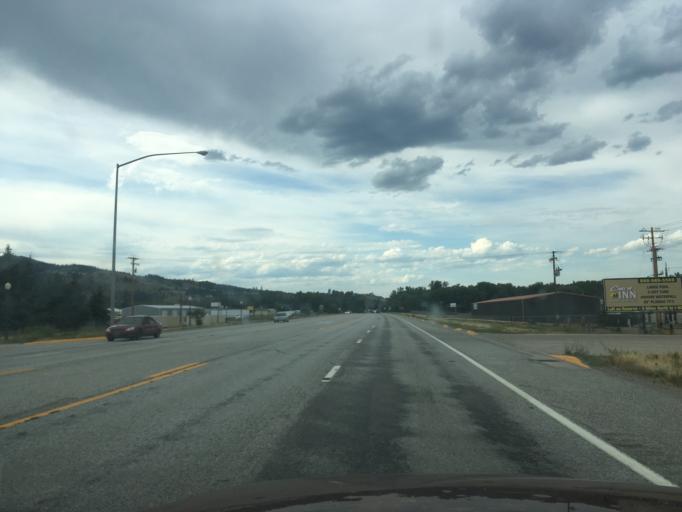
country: US
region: Montana
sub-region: Missoula County
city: Lolo
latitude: 46.7430
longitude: -114.0816
